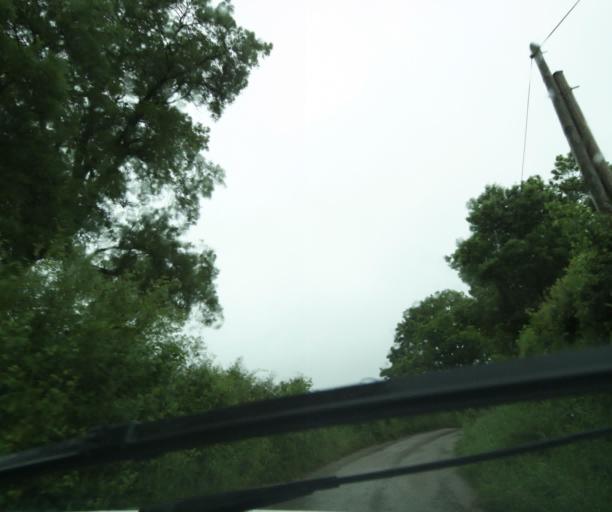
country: FR
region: Bourgogne
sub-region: Departement de Saone-et-Loire
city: Charolles
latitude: 46.3866
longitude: 4.3524
